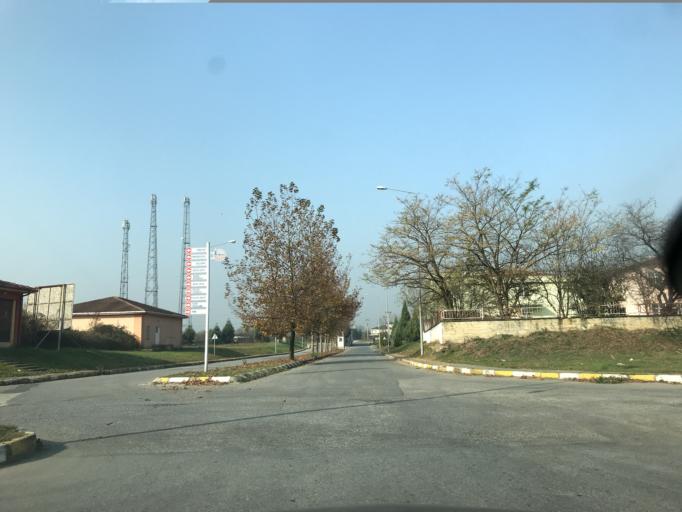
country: TR
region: Duzce
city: Duzce
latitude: 40.7887
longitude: 31.1328
